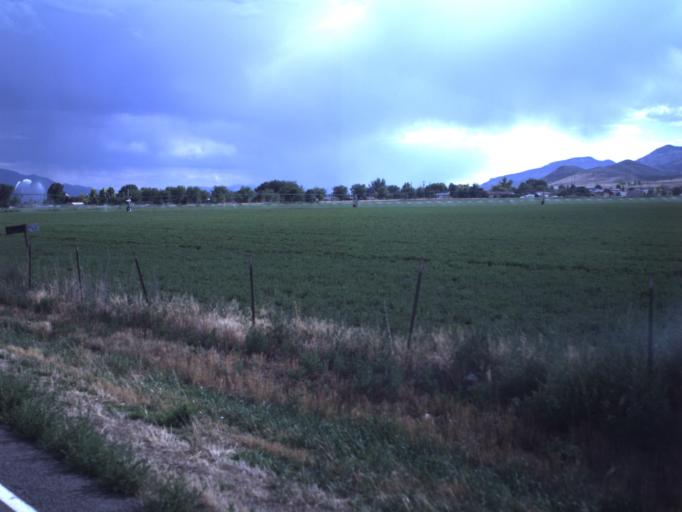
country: US
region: Utah
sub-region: Sevier County
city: Aurora
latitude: 38.9305
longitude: -111.9343
